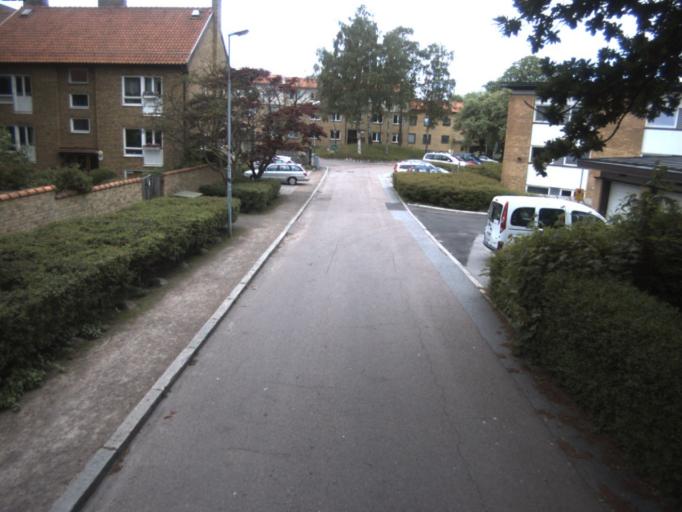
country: SE
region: Skane
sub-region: Helsingborg
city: Helsingborg
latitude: 56.0509
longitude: 12.6949
